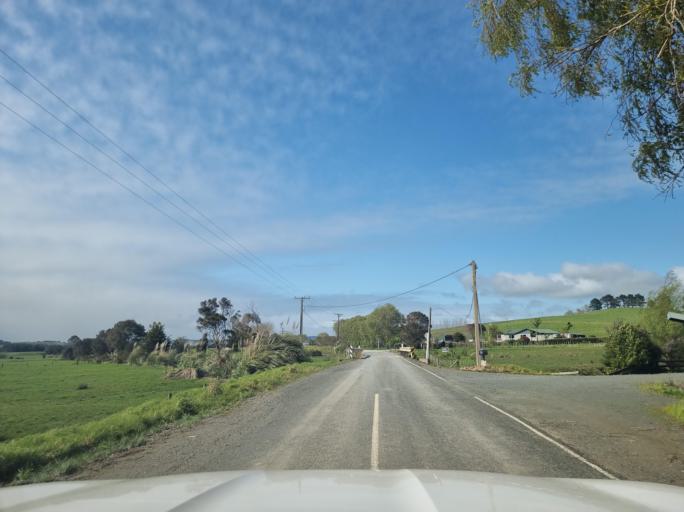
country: NZ
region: Auckland
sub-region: Auckland
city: Wellsford
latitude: -36.1139
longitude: 174.4999
